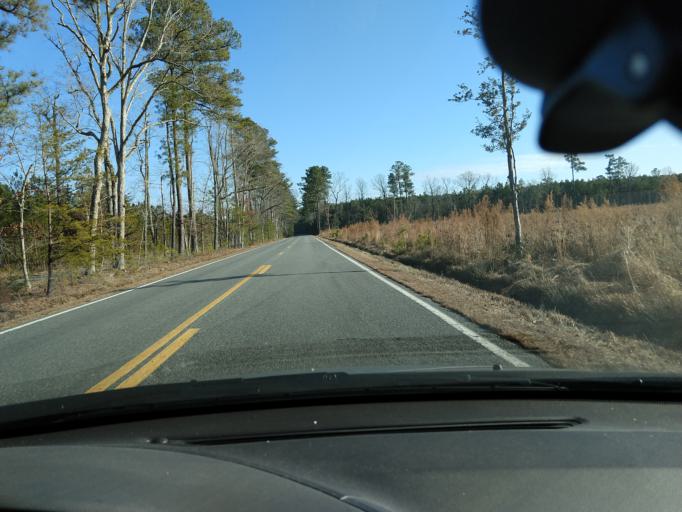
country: US
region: Virginia
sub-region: Charles City County
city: Charles City
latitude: 37.3032
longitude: -76.9545
